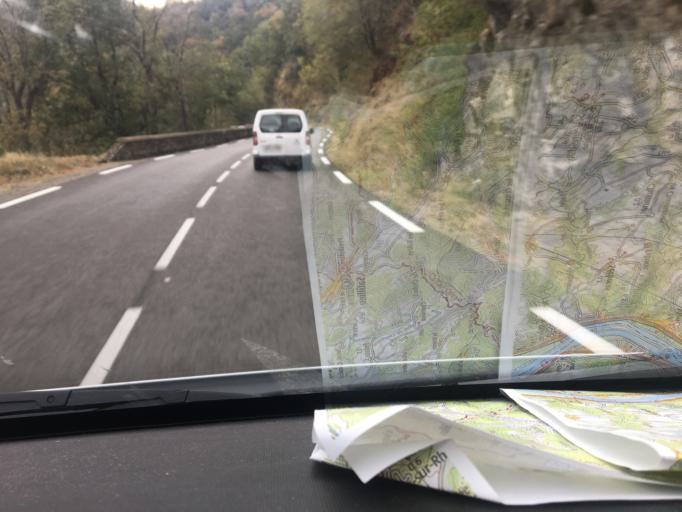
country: FR
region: Rhone-Alpes
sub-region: Departement de l'Ardeche
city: Saint-Jean-de-Muzols
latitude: 45.0574
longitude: 4.7689
